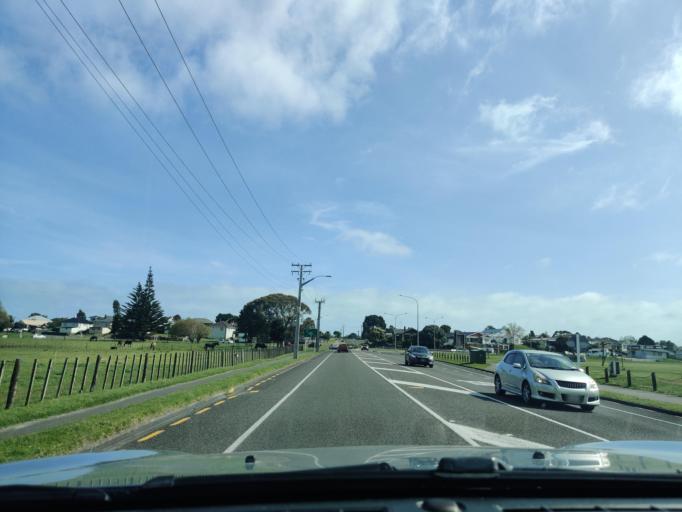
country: NZ
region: Manawatu-Wanganui
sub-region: Wanganui District
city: Wanganui
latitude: -39.9317
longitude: 175.0299
